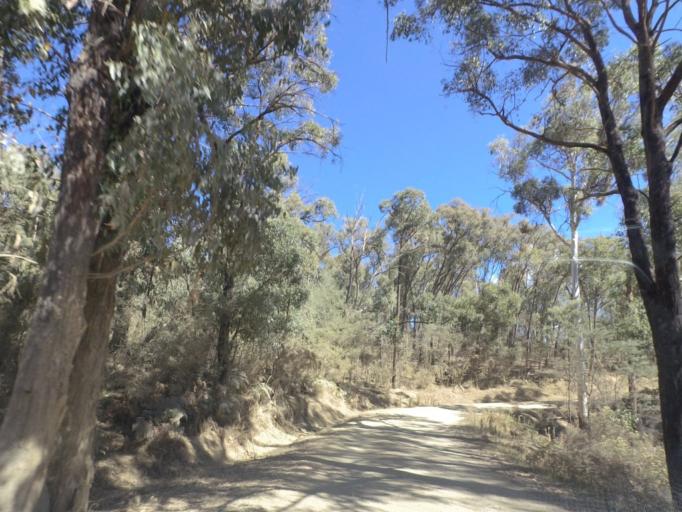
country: AU
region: Victoria
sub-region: Murrindindi
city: Alexandra
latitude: -37.3186
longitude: 145.8110
